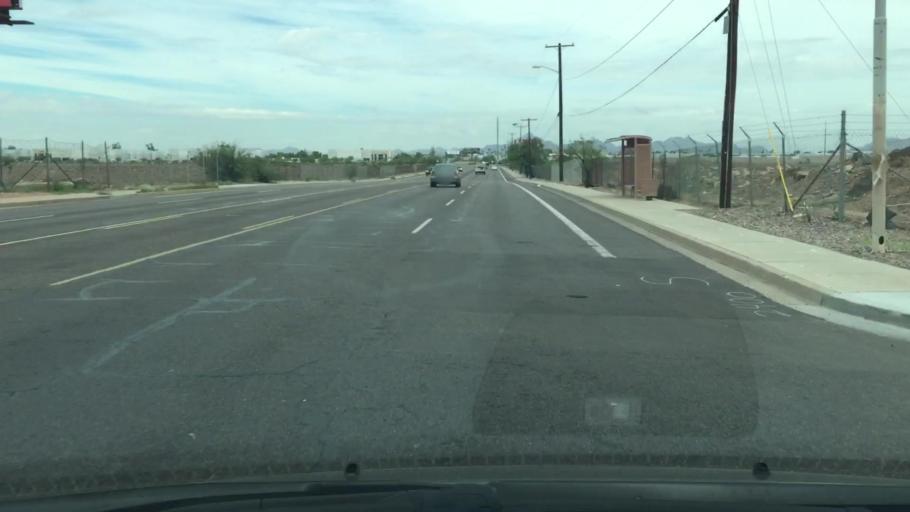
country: US
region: Arizona
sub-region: Maricopa County
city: Phoenix
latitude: 33.4108
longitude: -112.0296
